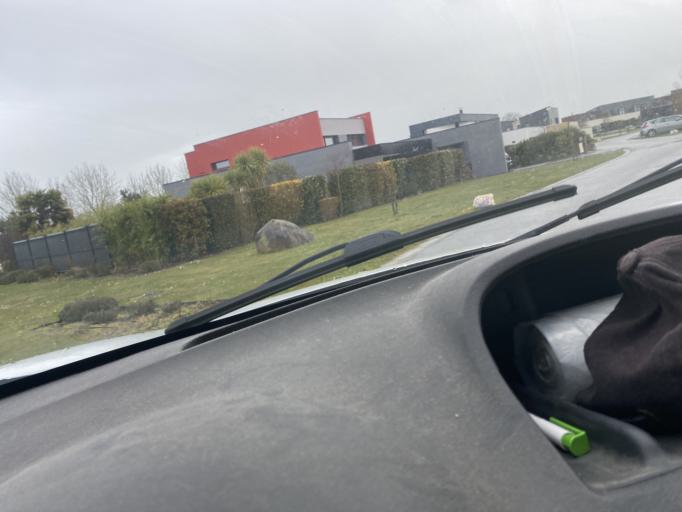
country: FR
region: Brittany
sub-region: Departement d'Ille-et-Vilaine
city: La Chapelle-des-Fougeretz
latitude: 48.1972
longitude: -1.7181
